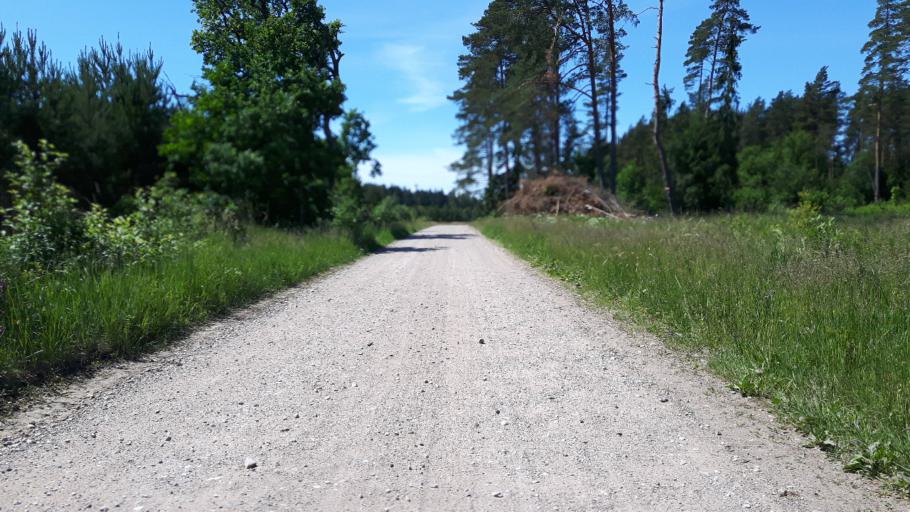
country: LV
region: Kandava
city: Kandava
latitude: 57.0413
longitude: 22.8156
